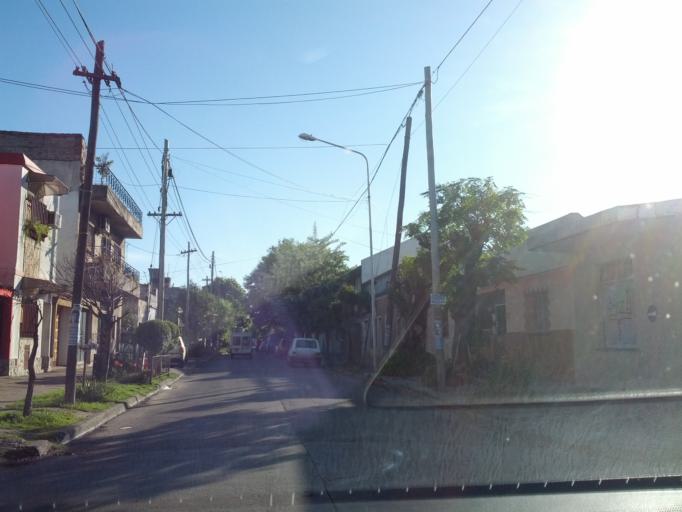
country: AR
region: Buenos Aires
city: San Justo
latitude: -34.6617
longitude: -58.5325
